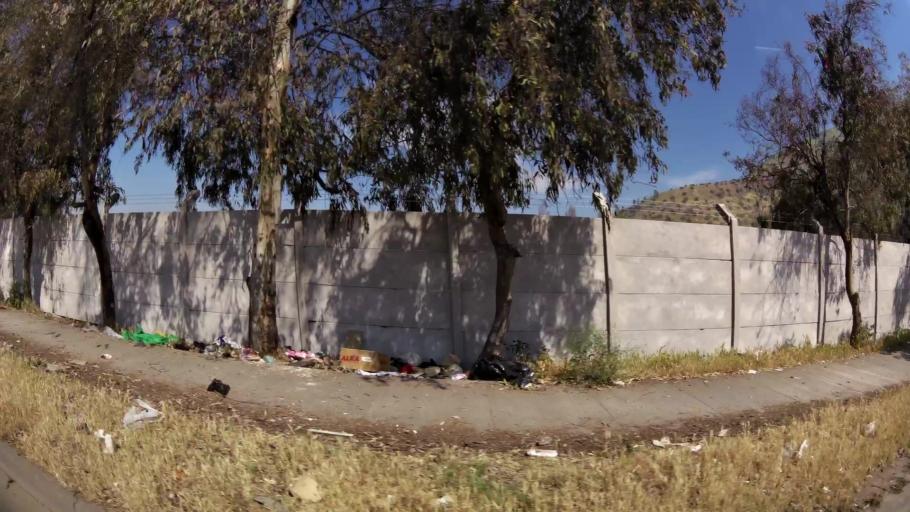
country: CL
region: Santiago Metropolitan
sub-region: Provincia de Santiago
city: Lo Prado
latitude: -33.3959
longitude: -70.7007
